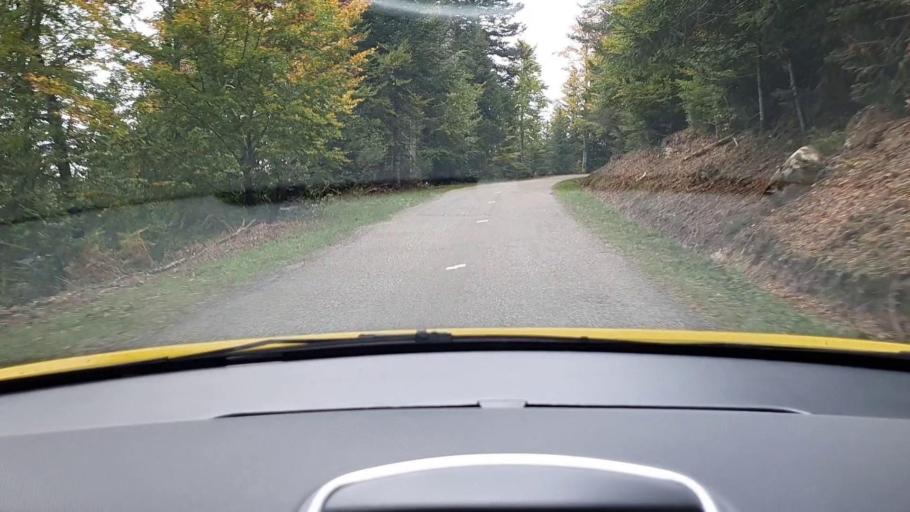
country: FR
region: Languedoc-Roussillon
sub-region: Departement de la Lozere
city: Meyrueis
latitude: 44.1004
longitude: 3.4737
